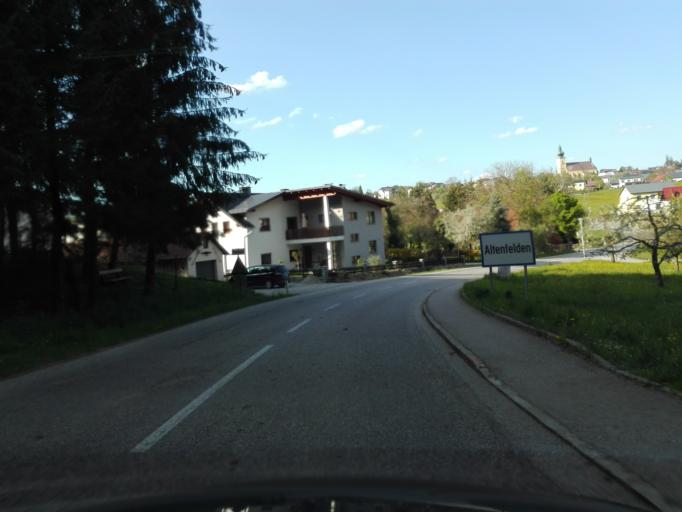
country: AT
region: Upper Austria
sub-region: Politischer Bezirk Rohrbach
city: Kleinzell im Muehlkreis
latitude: 48.4801
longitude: 13.9628
